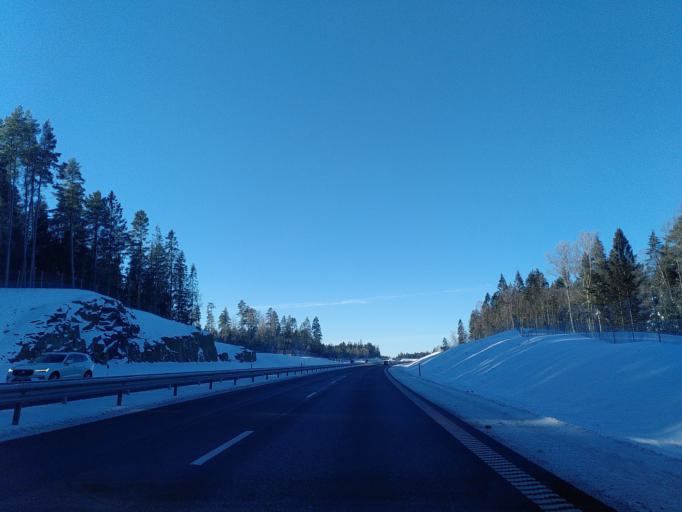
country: SE
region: Vaestra Goetaland
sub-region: Vargarda Kommun
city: Jonstorp
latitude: 57.9967
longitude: 12.7433
